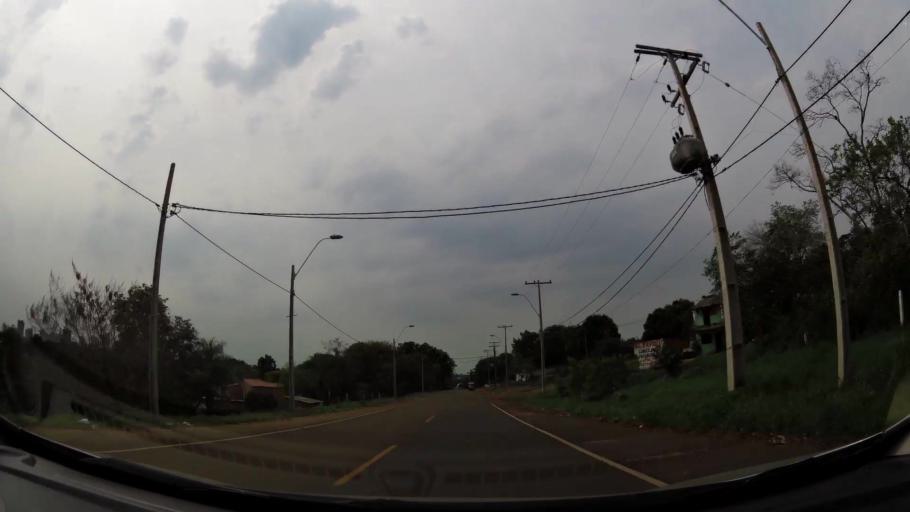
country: BR
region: Parana
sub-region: Foz Do Iguacu
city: Foz do Iguacu
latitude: -25.5511
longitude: -54.6047
